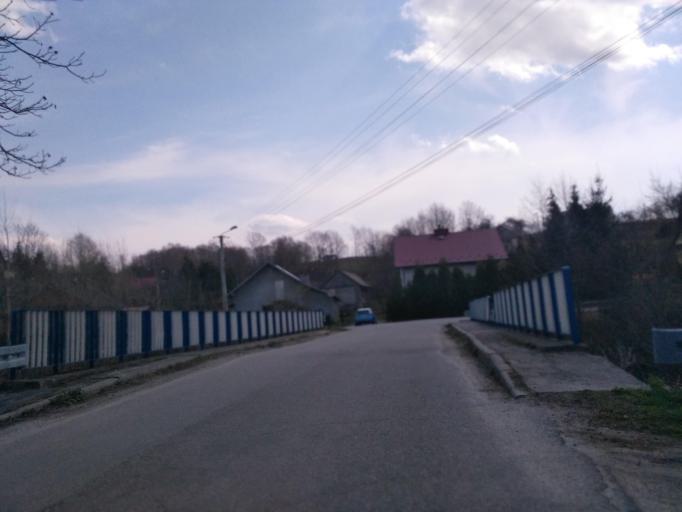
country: PL
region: Subcarpathian Voivodeship
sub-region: Powiat ropczycko-sedziszowski
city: Sedziszow Malopolski
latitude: 50.0417
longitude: 21.7041
